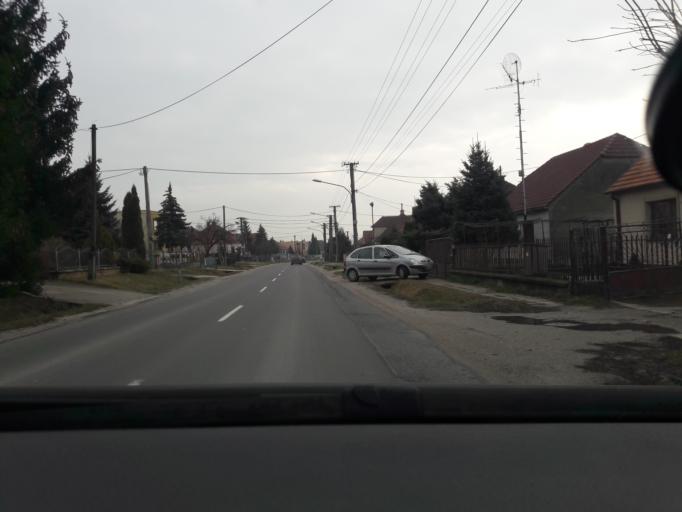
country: SK
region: Trnavsky
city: Smolenice
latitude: 48.4709
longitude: 17.4371
